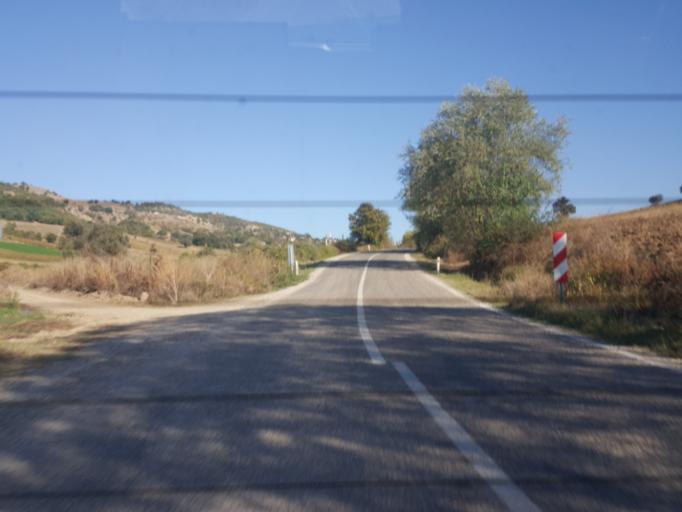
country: TR
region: Amasya
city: Tasova
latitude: 40.7173
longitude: 36.3114
